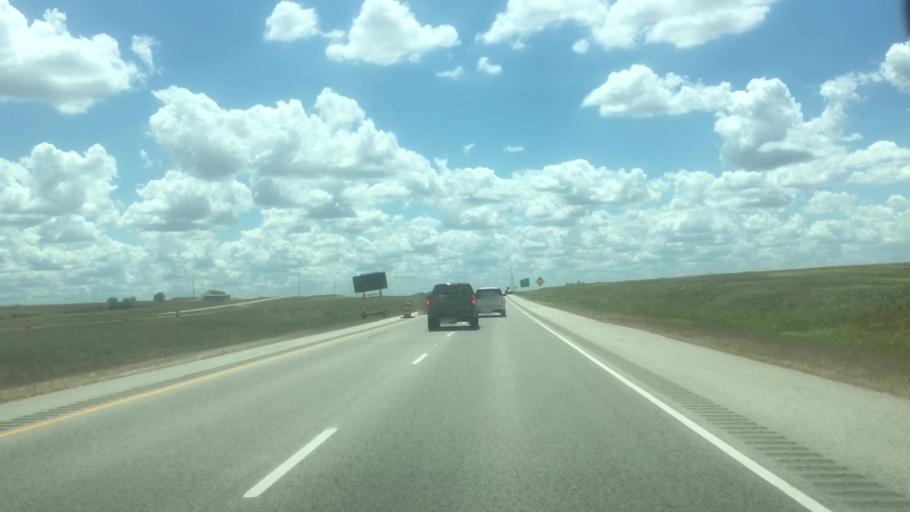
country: US
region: Texas
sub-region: Caldwell County
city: Martindale
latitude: 29.7929
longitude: -97.7831
